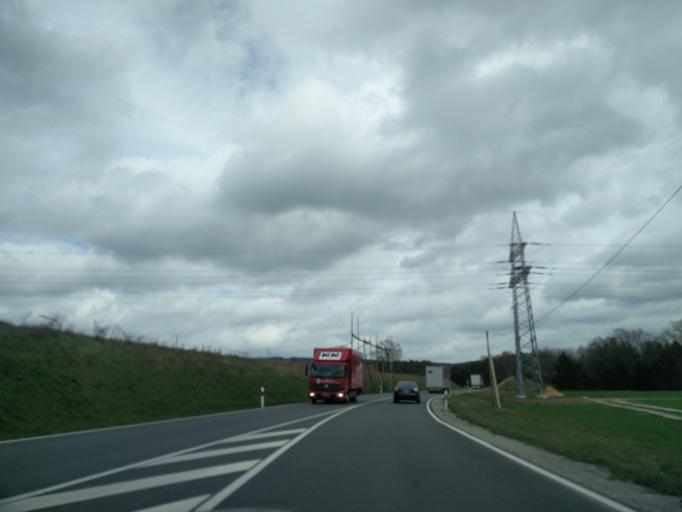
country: DE
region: North Rhine-Westphalia
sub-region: Regierungsbezirk Detmold
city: Steinhagen
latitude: 52.0261
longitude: 8.3903
